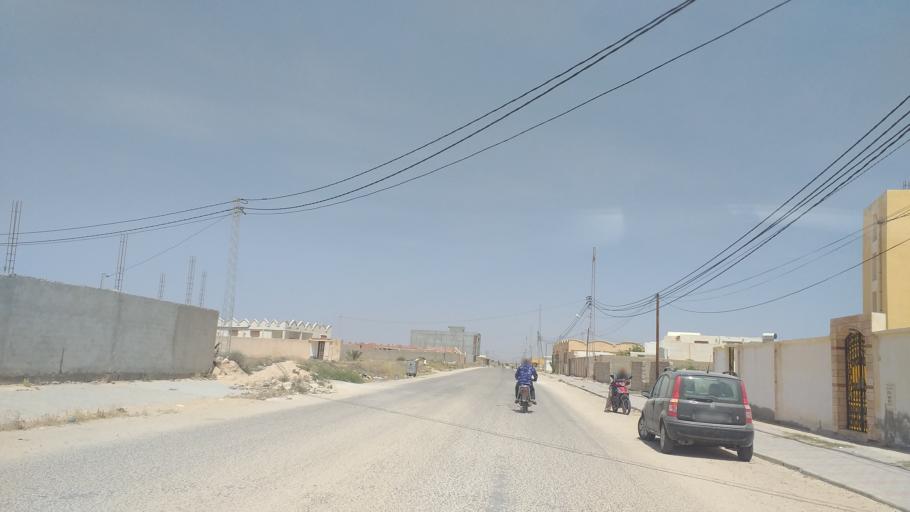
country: TN
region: Qabis
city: Gabes
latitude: 33.9522
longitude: 10.0680
